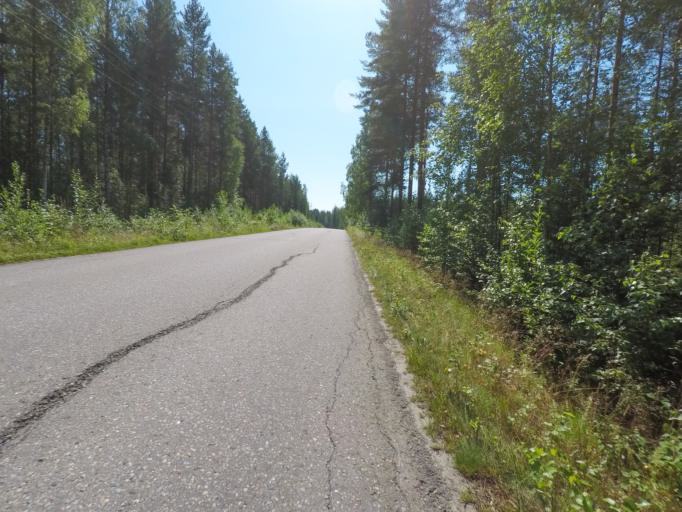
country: FI
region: Southern Savonia
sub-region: Mikkeli
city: Puumala
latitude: 61.4407
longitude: 28.1653
